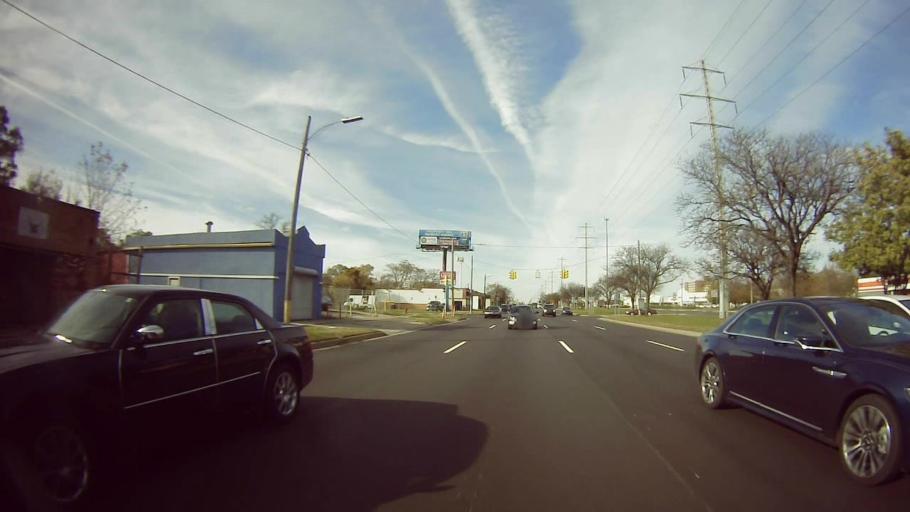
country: US
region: Michigan
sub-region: Oakland County
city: Ferndale
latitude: 42.4457
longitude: -83.1582
